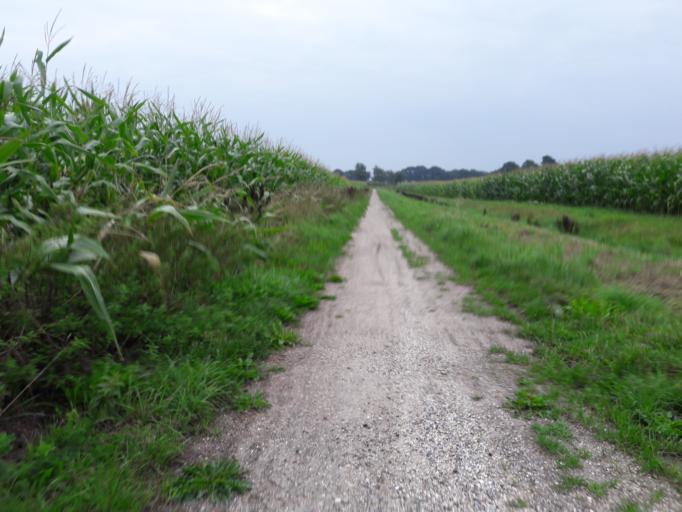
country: NL
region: Drenthe
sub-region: Gemeente Borger-Odoorn
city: Borger
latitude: 52.9430
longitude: 6.8159
